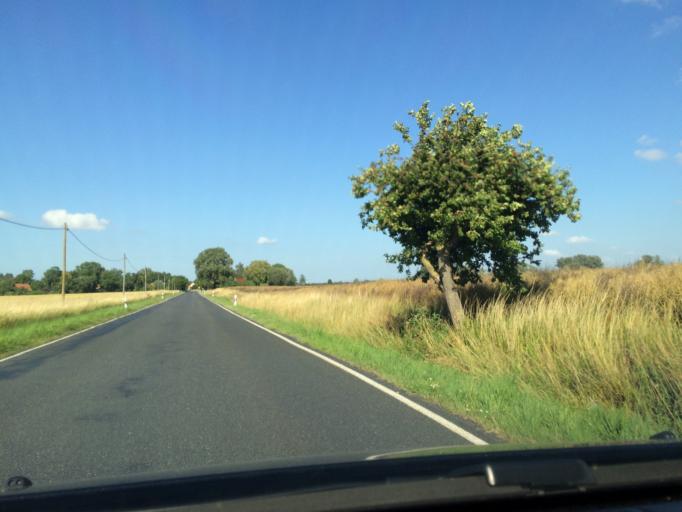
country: DE
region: Mecklenburg-Vorpommern
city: Niepars
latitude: 54.3412
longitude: 12.8877
